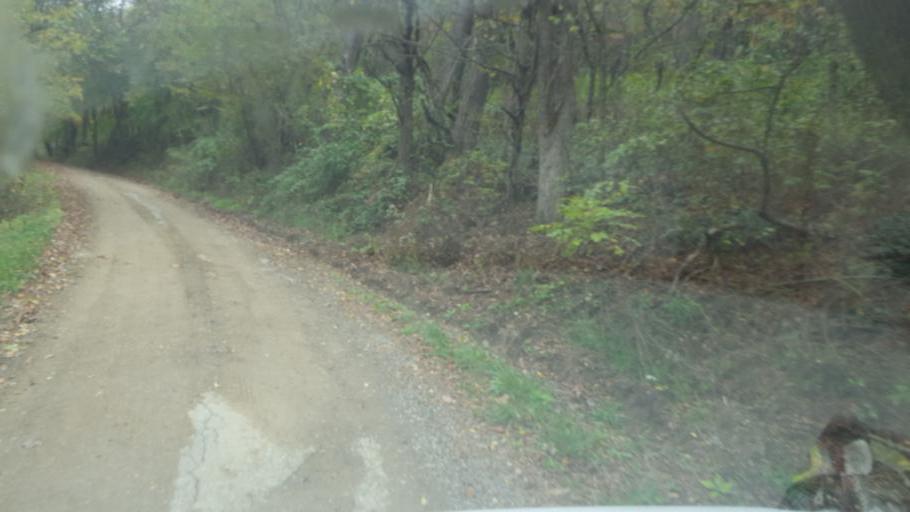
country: US
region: Ohio
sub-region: Wayne County
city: Shreve
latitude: 40.5293
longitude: -82.0795
